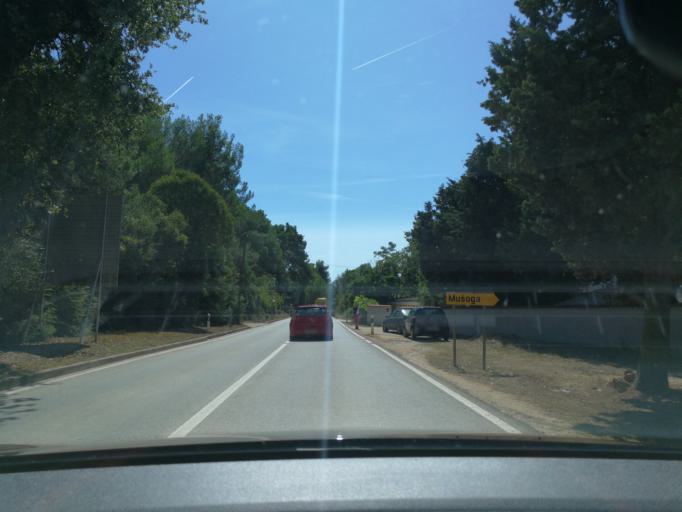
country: HR
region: Istarska
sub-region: Grad Pula
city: Pula
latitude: 44.8245
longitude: 13.8787
